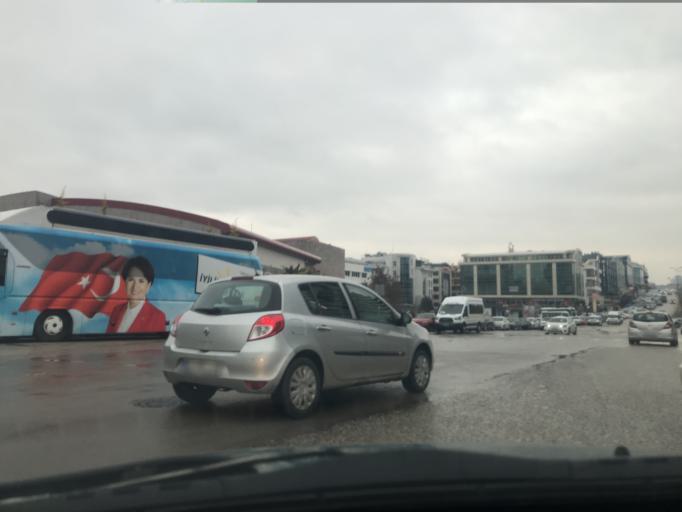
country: TR
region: Ankara
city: Batikent
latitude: 39.9103
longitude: 32.7639
